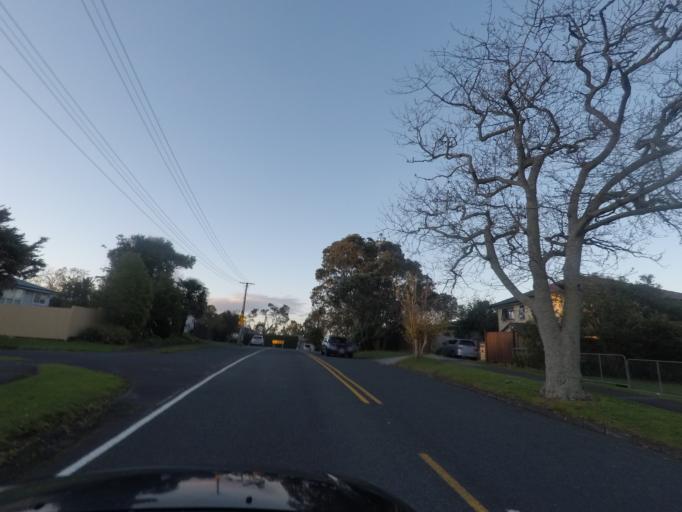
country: NZ
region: Auckland
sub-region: Auckland
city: Waitakere
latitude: -36.9063
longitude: 174.6674
